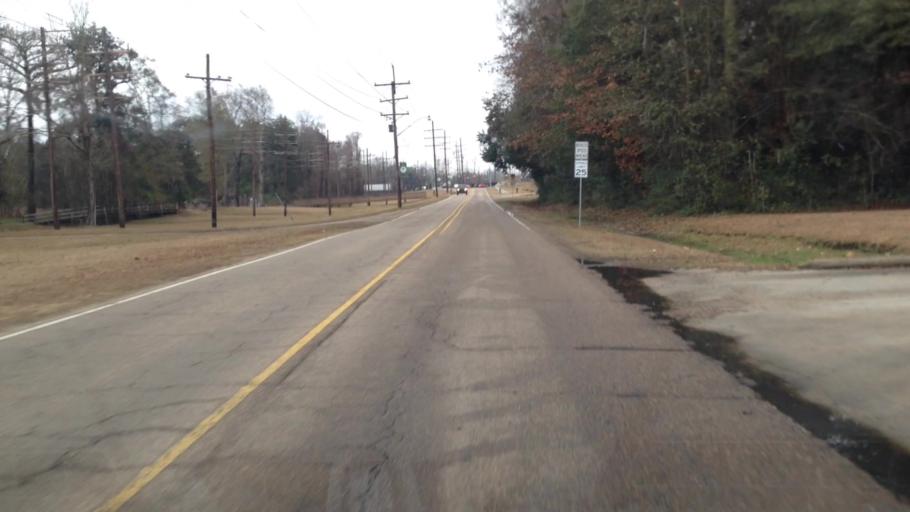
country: US
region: Louisiana
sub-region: Washington Parish
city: Bogalusa
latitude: 30.7824
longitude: -89.8696
